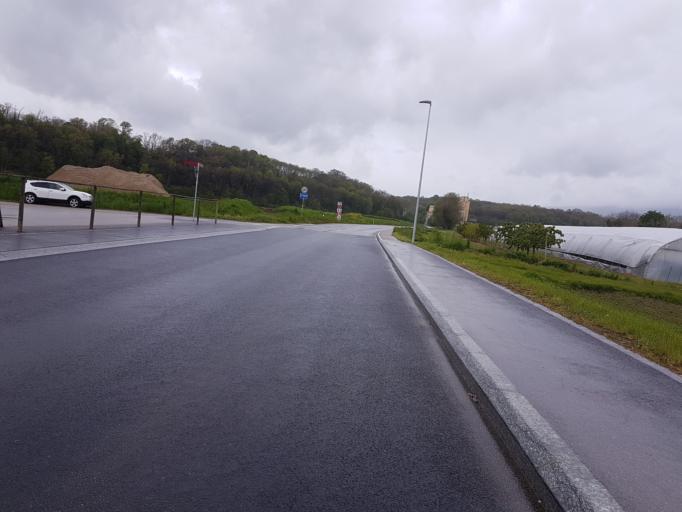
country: CH
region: Vaud
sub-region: Morges District
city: Orny
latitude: 46.6651
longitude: 6.5222
